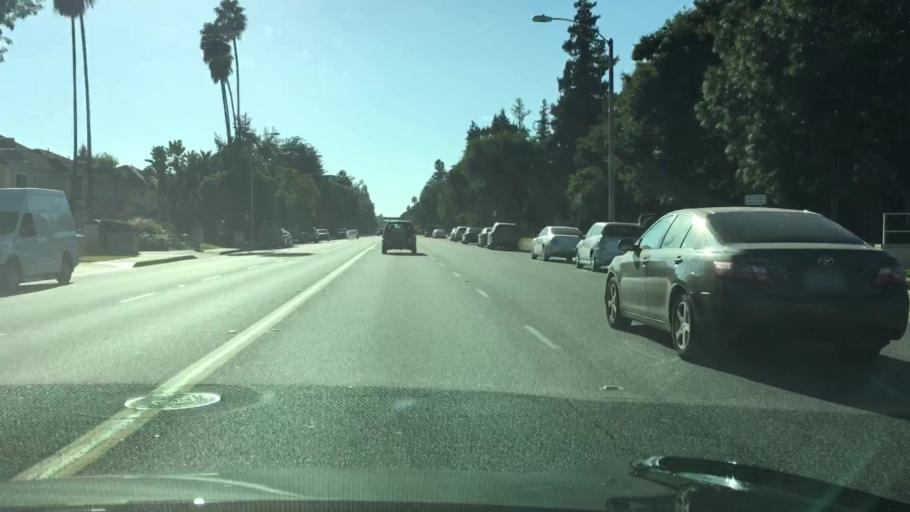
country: US
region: California
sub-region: Los Angeles County
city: Arcadia
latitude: 34.1273
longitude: -118.0471
